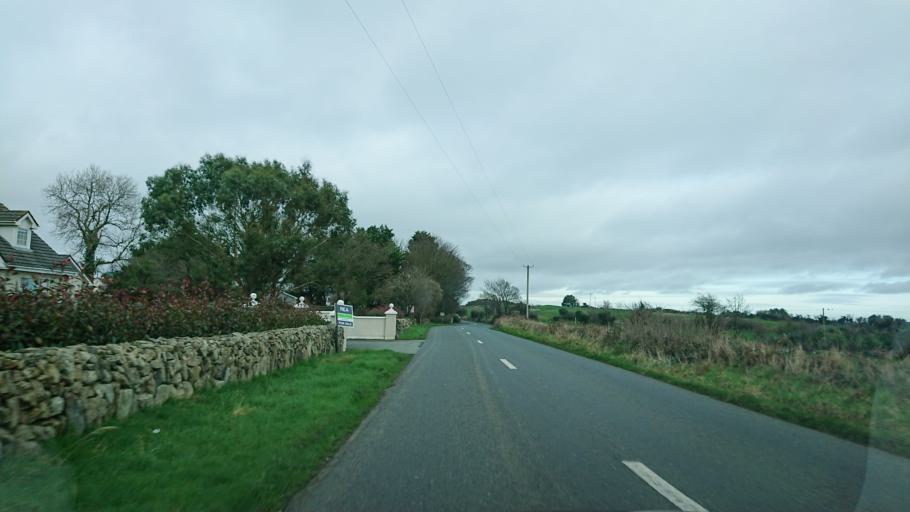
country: IE
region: Leinster
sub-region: Kilkenny
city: Mooncoin
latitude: 52.1942
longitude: -7.2740
